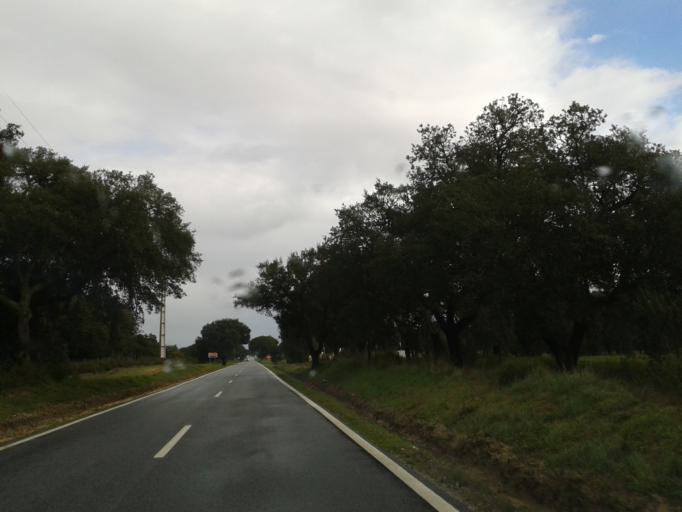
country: PT
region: Santarem
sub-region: Benavente
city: Poceirao
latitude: 38.8339
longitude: -8.7441
